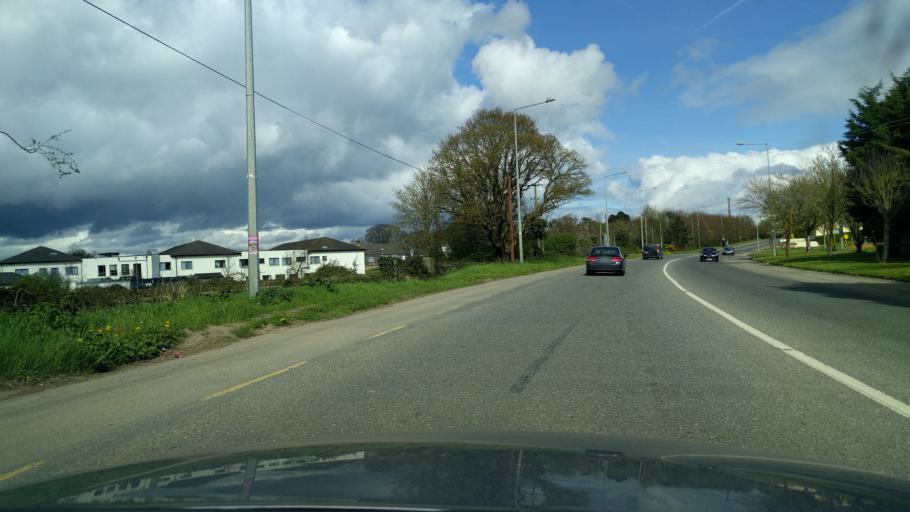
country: IE
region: Leinster
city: Balrothery
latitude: 53.5918
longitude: -6.1878
